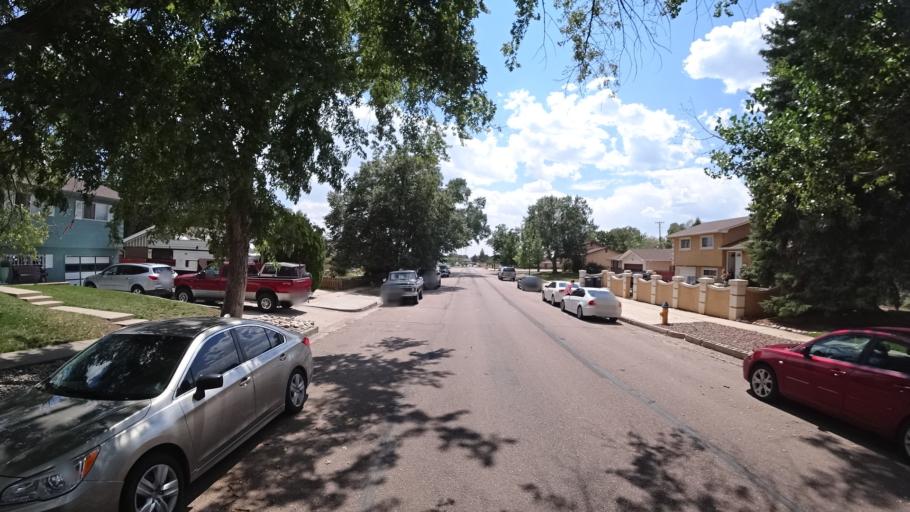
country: US
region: Colorado
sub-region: El Paso County
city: Colorado Springs
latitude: 38.8282
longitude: -104.7799
